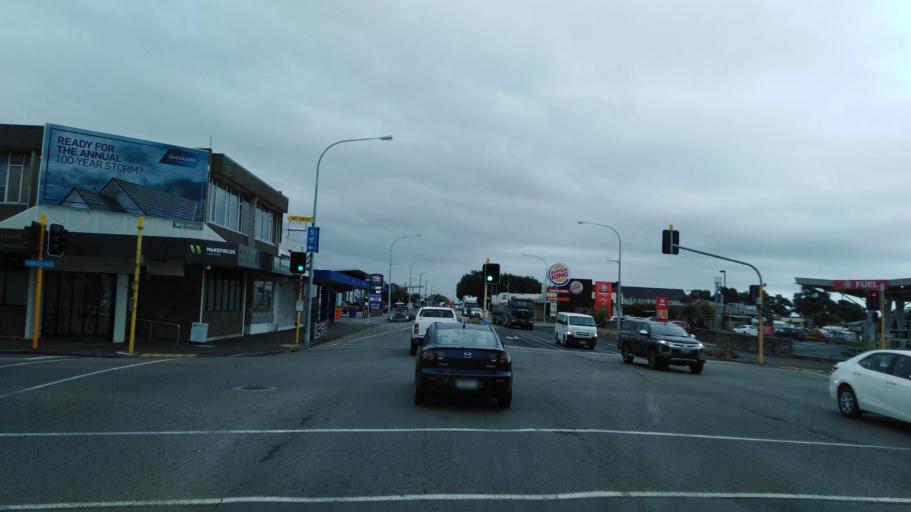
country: NZ
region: Manawatu-Wanganui
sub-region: Horowhenua District
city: Levin
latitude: -40.6235
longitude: 175.2850
